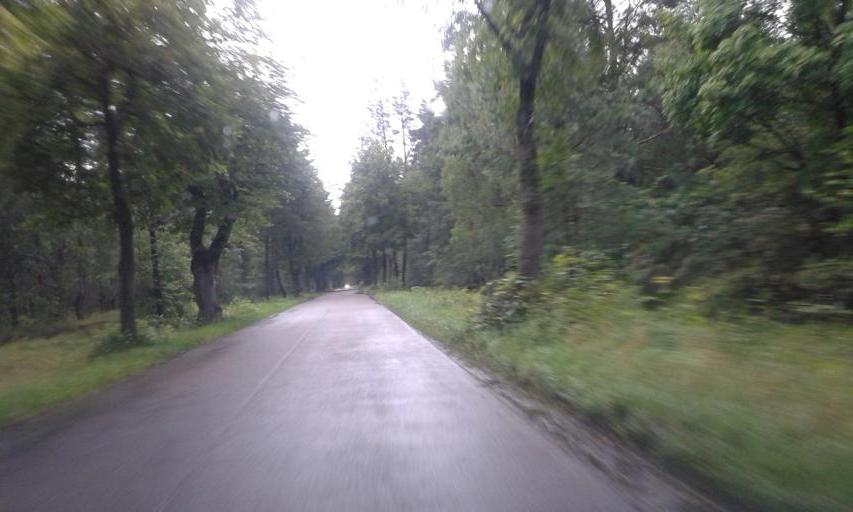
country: PL
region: West Pomeranian Voivodeship
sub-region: Powiat szczecinecki
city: Borne Sulinowo
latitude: 53.5046
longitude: 16.4985
